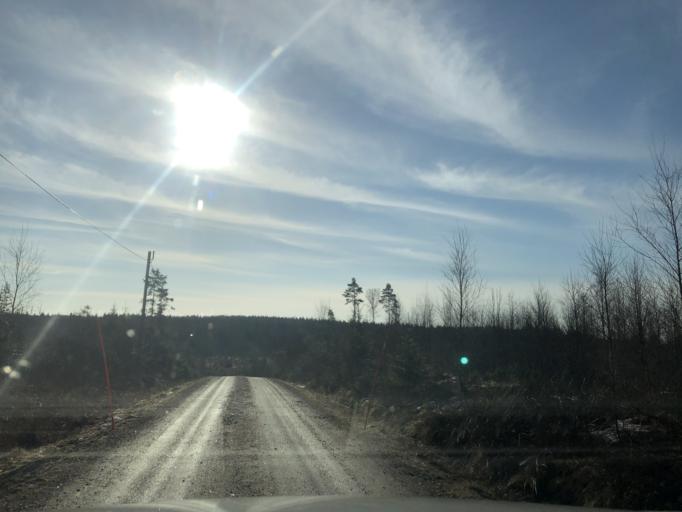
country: SE
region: Vaestra Goetaland
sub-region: Ulricehamns Kommun
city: Ulricehamn
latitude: 57.7931
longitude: 13.4672
